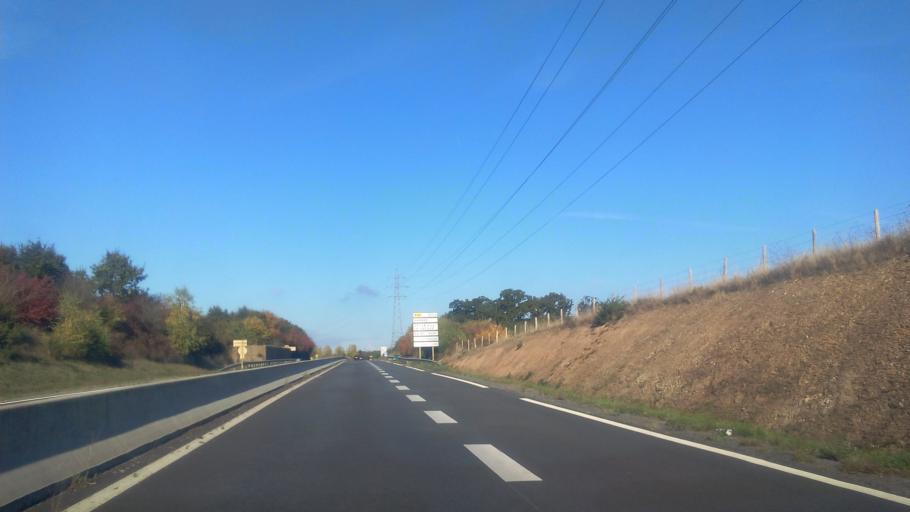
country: FR
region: Pays de la Loire
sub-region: Departement de la Loire-Atlantique
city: Saint-Nicolas-de-Redon
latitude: 47.6719
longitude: -2.0579
